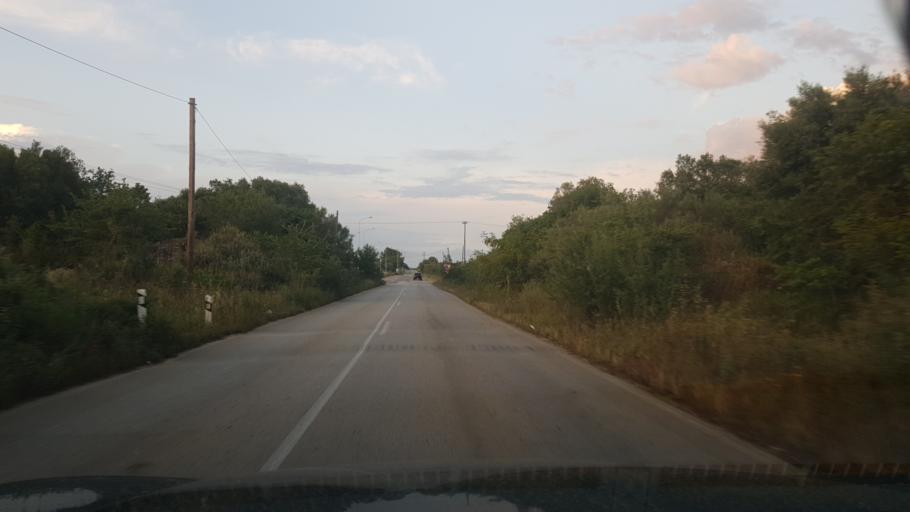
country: GR
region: West Greece
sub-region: Nomos Aitolias kai Akarnanias
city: Vonitsa
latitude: 38.8919
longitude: 20.8558
